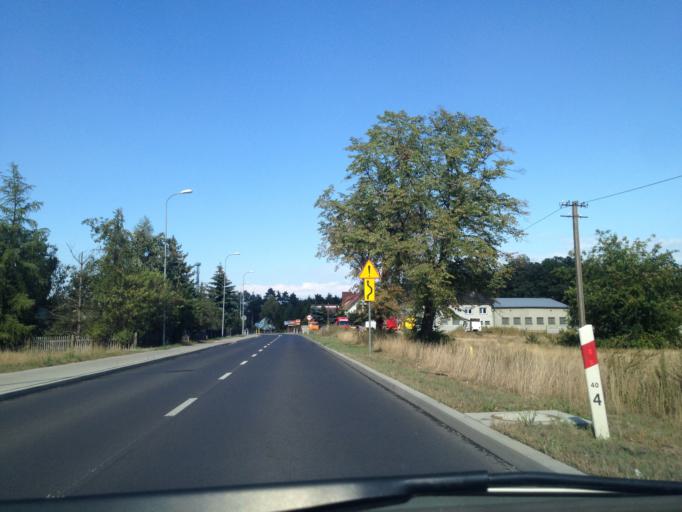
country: PL
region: Lubusz
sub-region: Powiat zaganski
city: Ilowa
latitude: 51.5136
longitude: 15.2113
